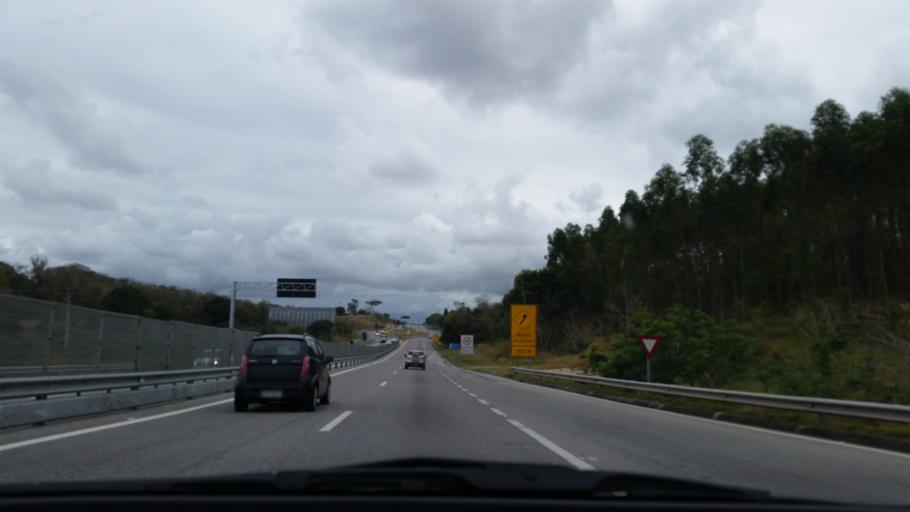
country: BR
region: Rio de Janeiro
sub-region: Araruama
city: Araruama
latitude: -22.8113
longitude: -42.3943
